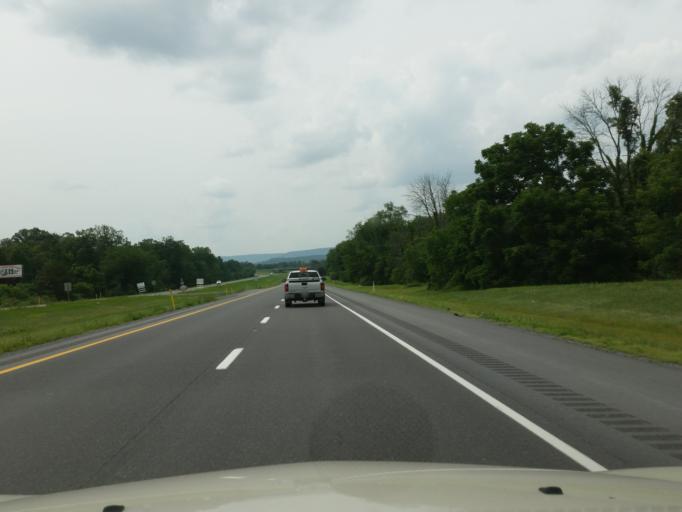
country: US
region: Pennsylvania
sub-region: Juniata County
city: Mifflintown
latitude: 40.5477
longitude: -77.3529
